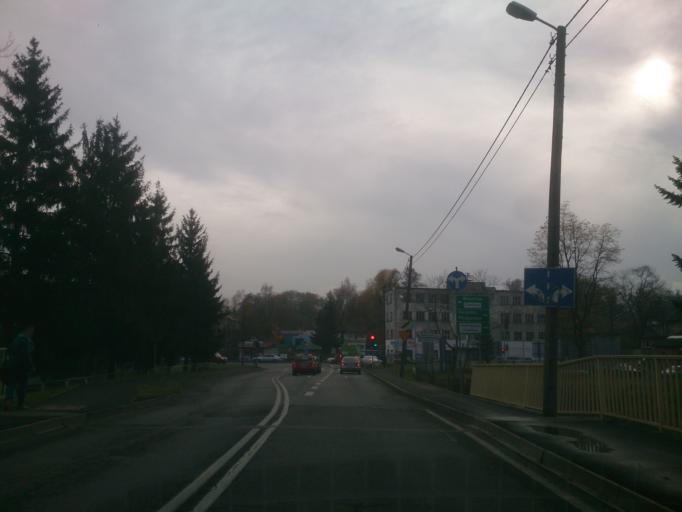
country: PL
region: Lower Silesian Voivodeship
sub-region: Jelenia Gora
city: Cieplice Slaskie Zdroj
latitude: 50.8681
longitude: 15.6924
